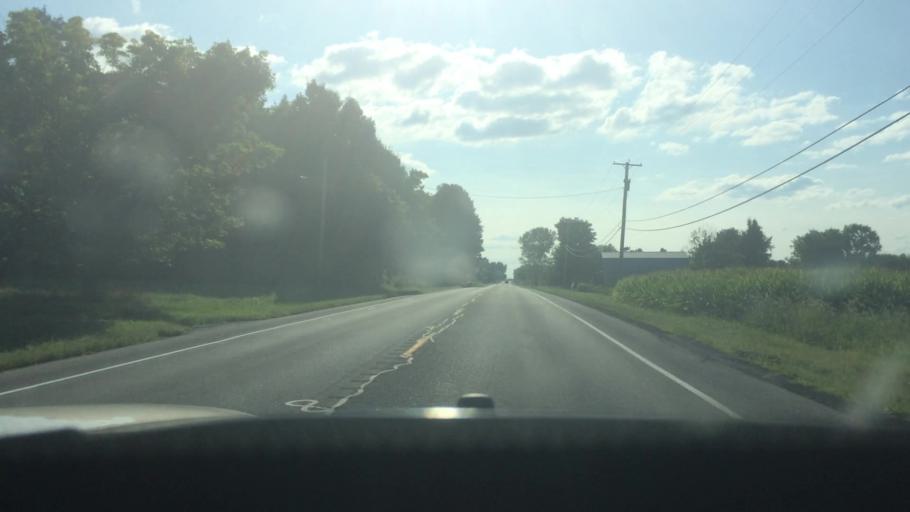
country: US
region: New York
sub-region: St. Lawrence County
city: Hannawa Falls
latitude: 44.6914
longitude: -74.6879
